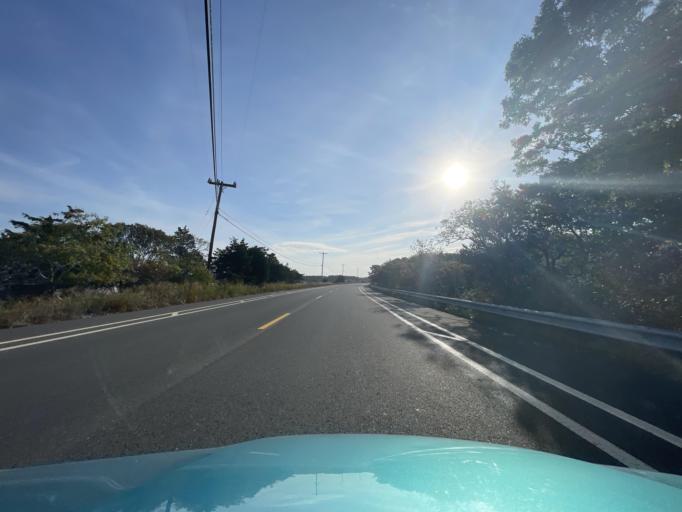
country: US
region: Massachusetts
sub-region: Bristol County
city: Head of Westport
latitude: 41.5096
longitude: -71.0575
